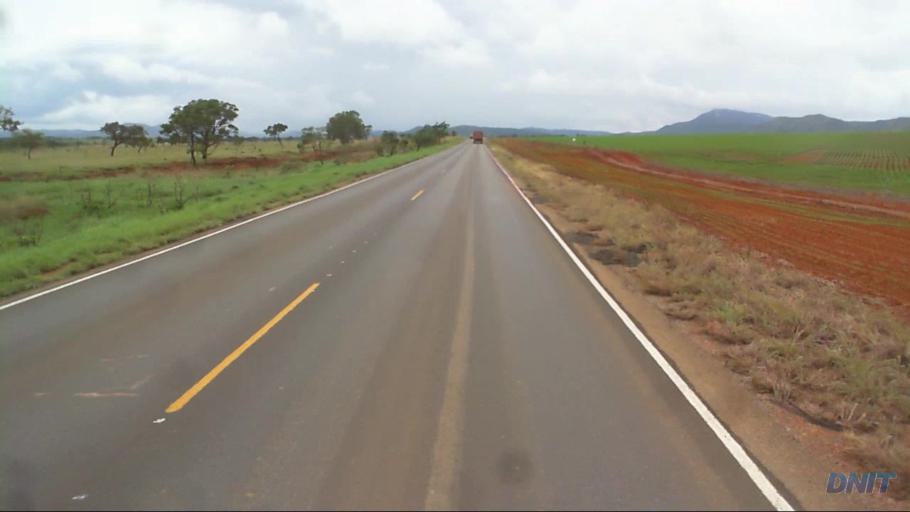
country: BR
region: Goias
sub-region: Padre Bernardo
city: Padre Bernardo
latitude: -15.3350
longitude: -48.2332
